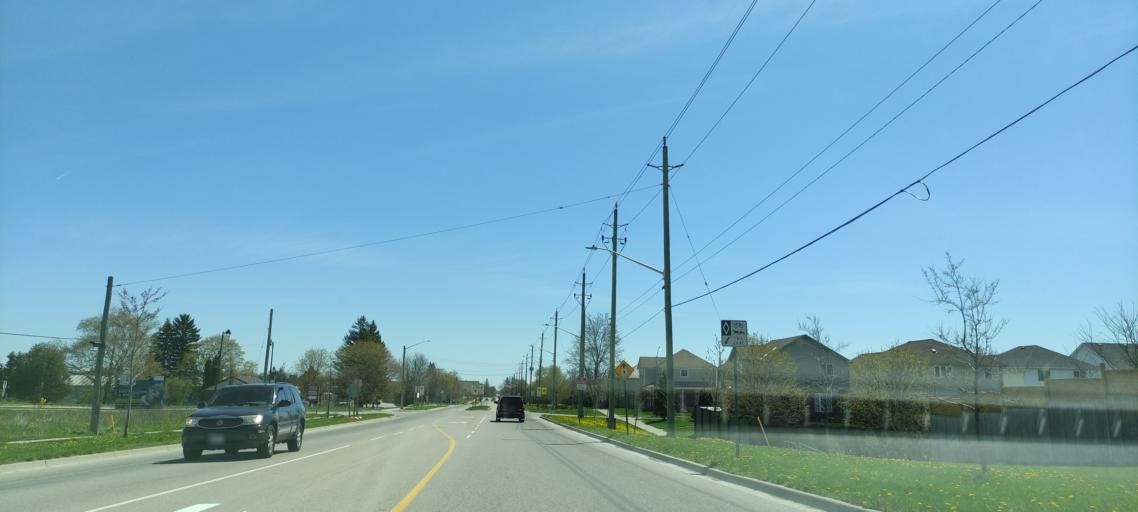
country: CA
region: Ontario
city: Waterloo
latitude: 43.6014
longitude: -80.5734
